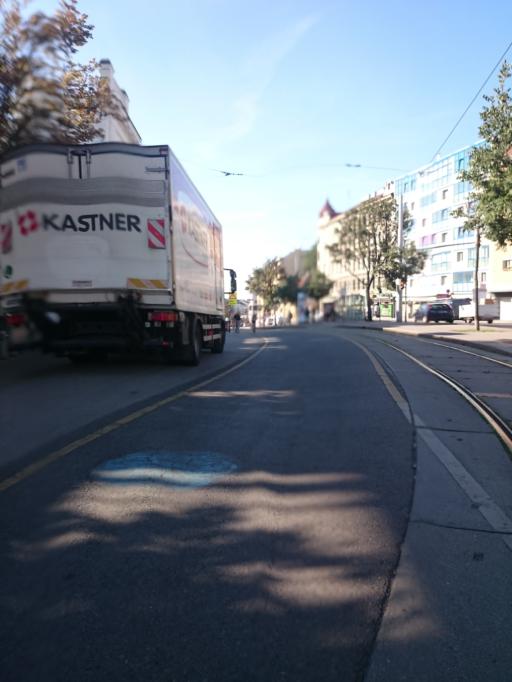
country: AT
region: Vienna
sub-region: Wien Stadt
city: Vienna
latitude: 48.2120
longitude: 16.3391
